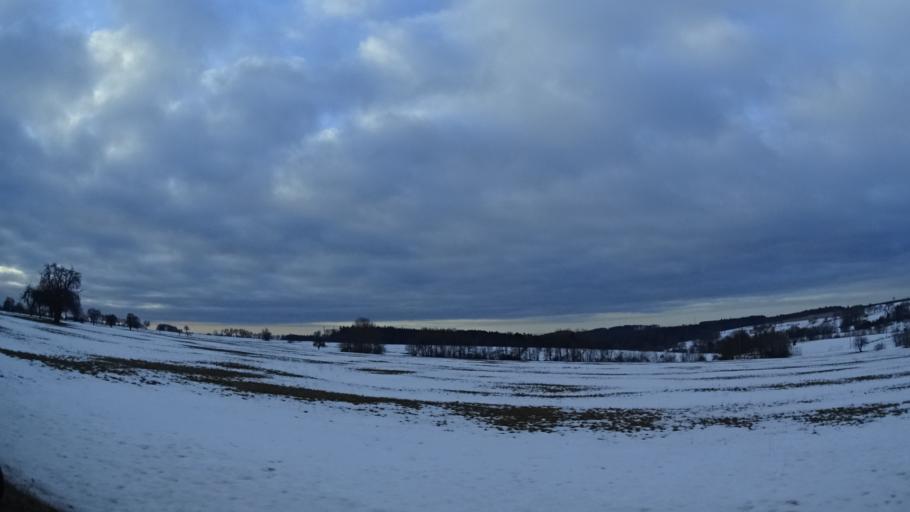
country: DE
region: Baden-Wuerttemberg
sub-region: Karlsruhe Region
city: Zwingenberg
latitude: 49.4640
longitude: 9.0892
